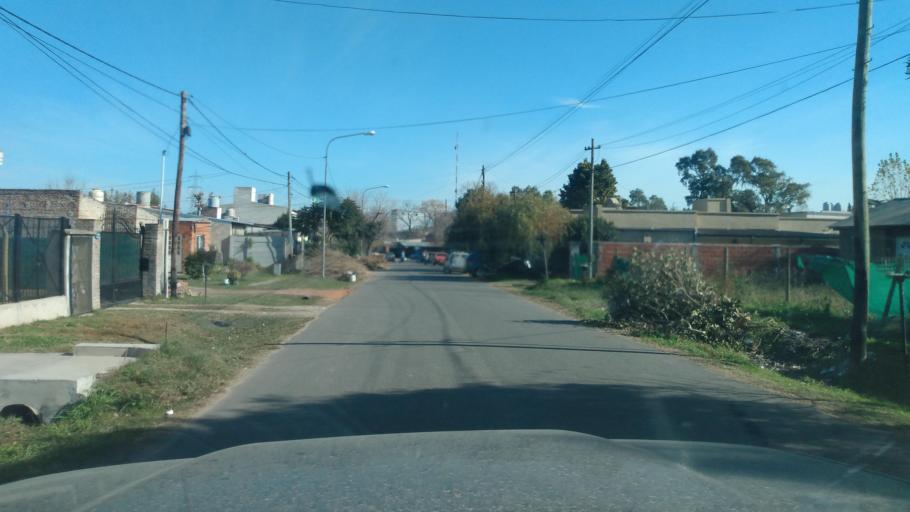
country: AR
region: Buenos Aires
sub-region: Partido de Lujan
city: Lujan
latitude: -34.5846
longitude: -59.1106
